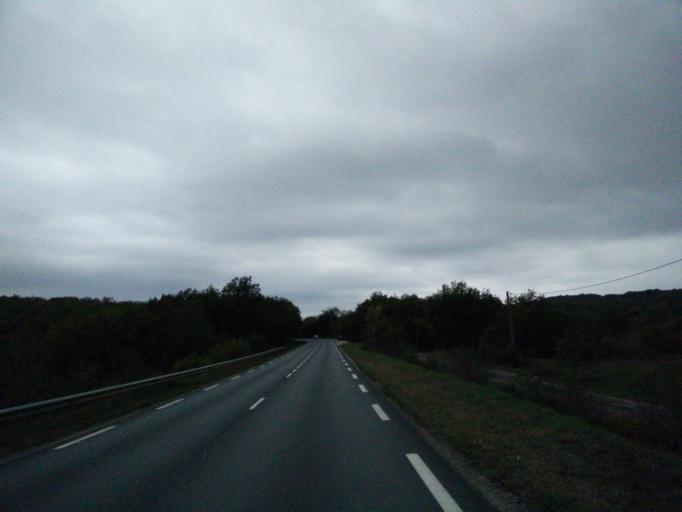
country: FR
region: Midi-Pyrenees
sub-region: Departement du Lot
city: Pradines
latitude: 44.5212
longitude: 1.3423
